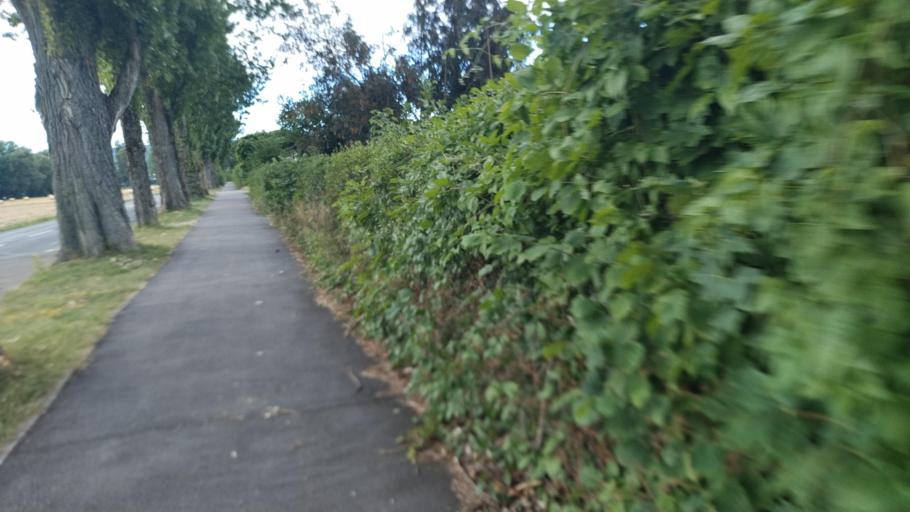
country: DE
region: Baden-Wuerttemberg
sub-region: Karlsruhe Region
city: Karlsruhe
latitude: 48.9784
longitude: 8.3961
